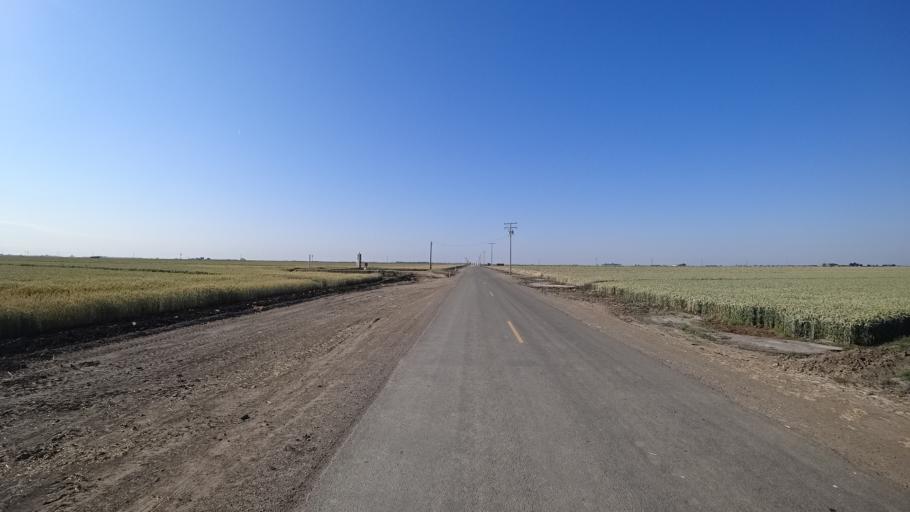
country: US
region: California
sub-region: Kings County
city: Home Garden
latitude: 36.2595
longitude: -119.5294
